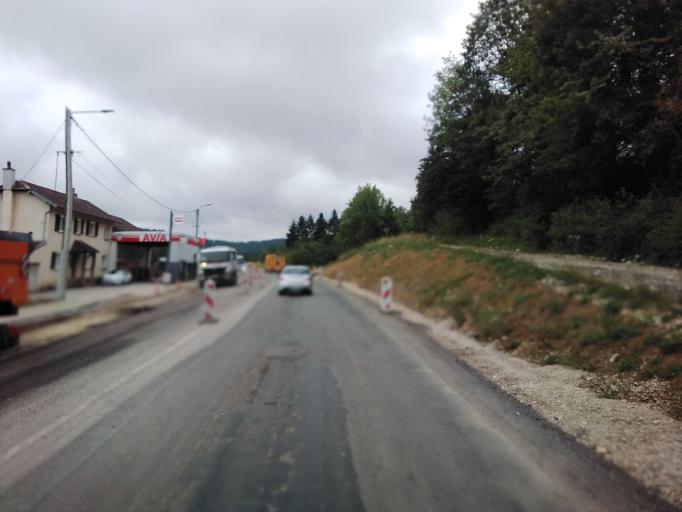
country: FR
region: Franche-Comte
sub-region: Departement de la Haute-Saone
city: Rioz
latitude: 47.4705
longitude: 6.0974
